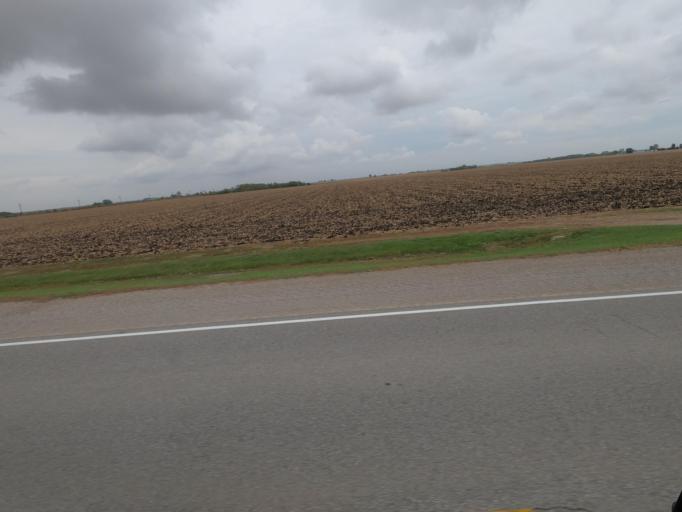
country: US
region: Iowa
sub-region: Wapello County
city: Ottumwa
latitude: 40.9870
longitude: -92.2368
